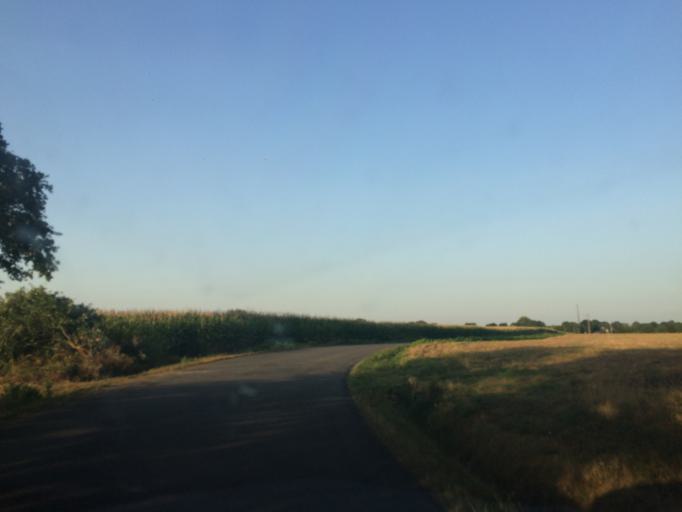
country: FR
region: Brittany
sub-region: Departement du Morbihan
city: Caden
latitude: 47.6363
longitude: -2.2503
